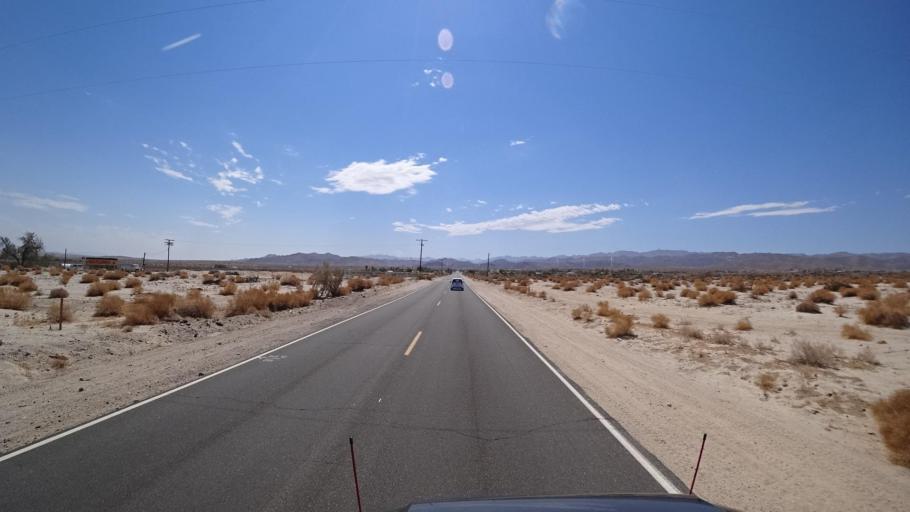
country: US
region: California
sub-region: Imperial County
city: Seeley
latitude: 32.7447
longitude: -115.9941
